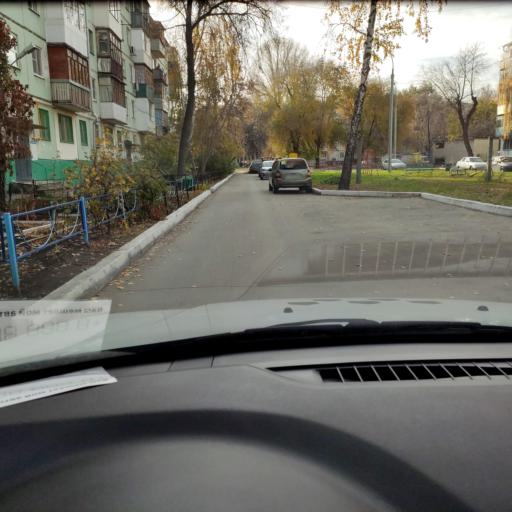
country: RU
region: Samara
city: Tol'yatti
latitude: 53.5134
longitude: 49.4375
